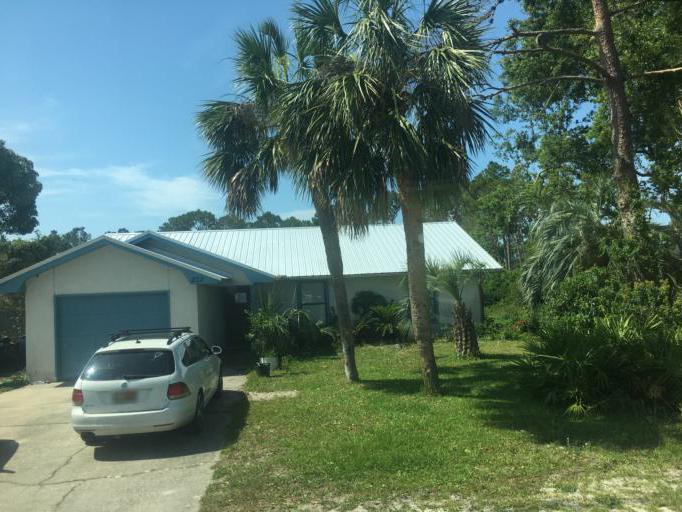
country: US
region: Florida
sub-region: Bay County
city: Upper Grand Lagoon
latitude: 30.1640
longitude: -85.7628
